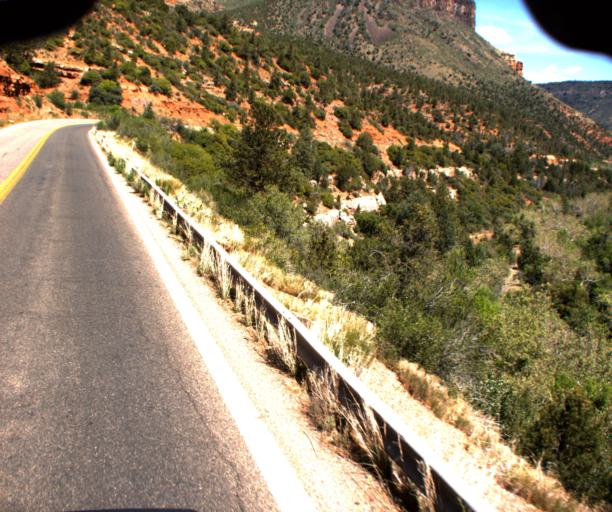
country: US
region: Arizona
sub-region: Coconino County
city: Sedona
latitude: 34.8892
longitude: -111.7337
